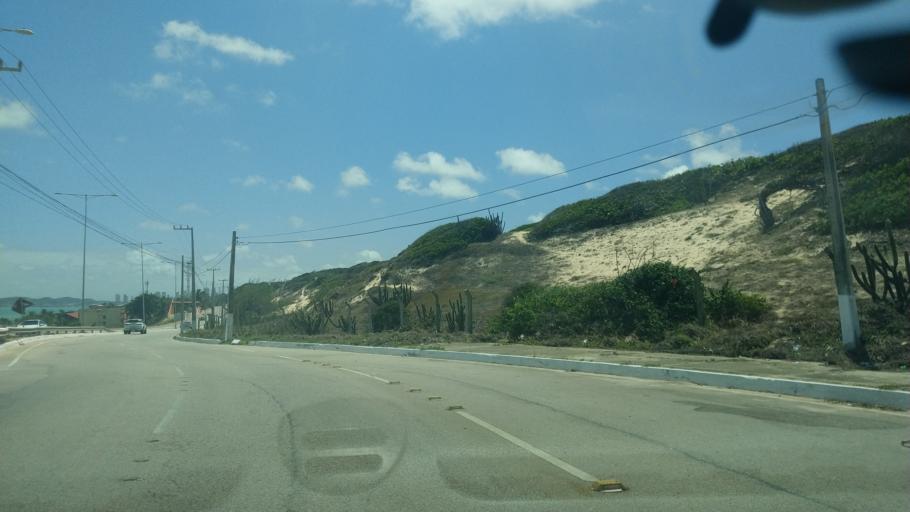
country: BR
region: Rio Grande do Norte
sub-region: Natal
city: Natal
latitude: -5.8232
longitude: -35.1834
